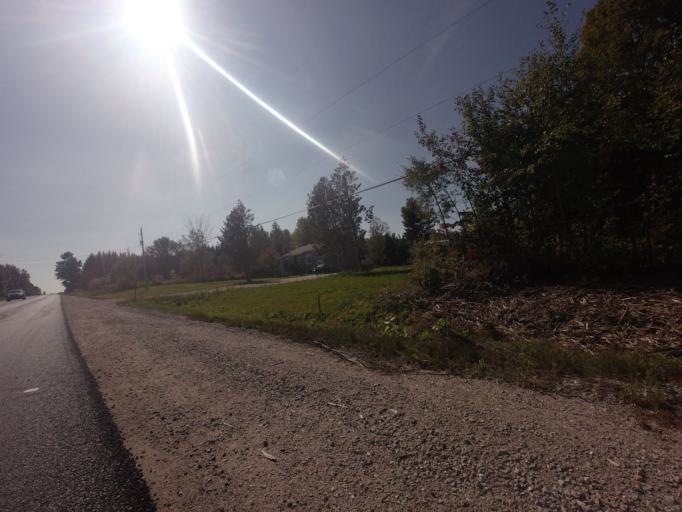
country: CA
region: Quebec
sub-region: Outaouais
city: Maniwaki
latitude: 46.5373
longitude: -75.8239
